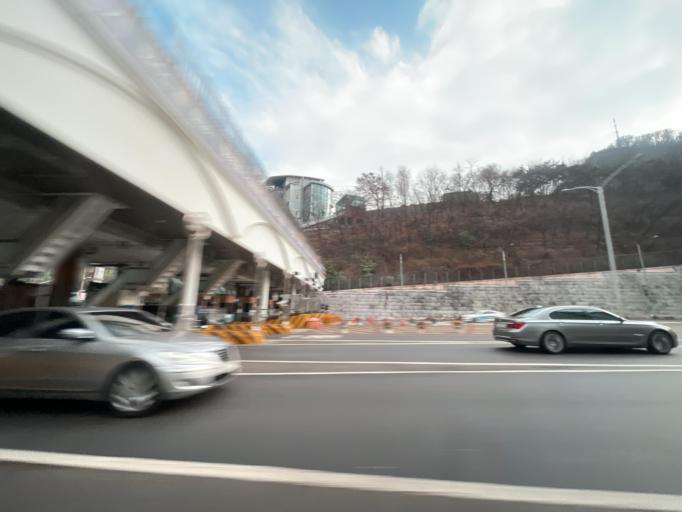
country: KR
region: Seoul
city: Seoul
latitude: 37.5565
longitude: 126.9830
